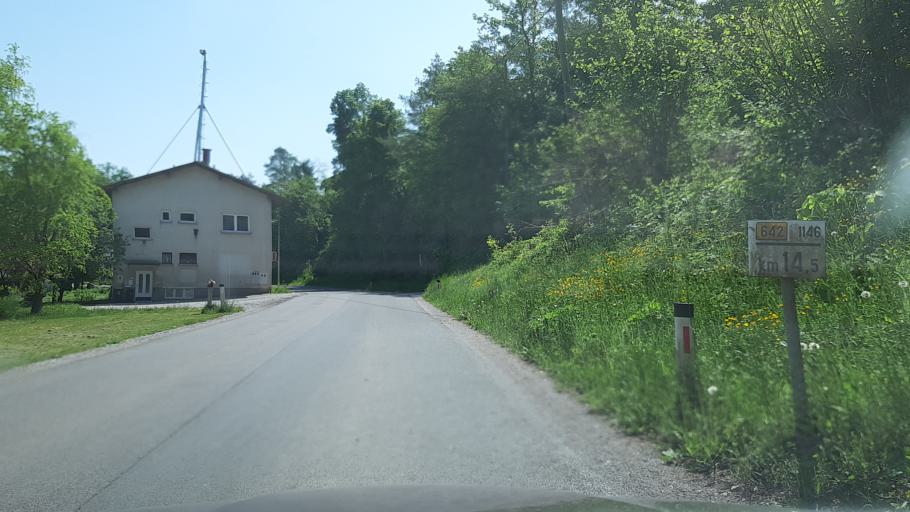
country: SI
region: Brezovica
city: Notranje Gorice
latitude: 45.9657
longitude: 14.3990
